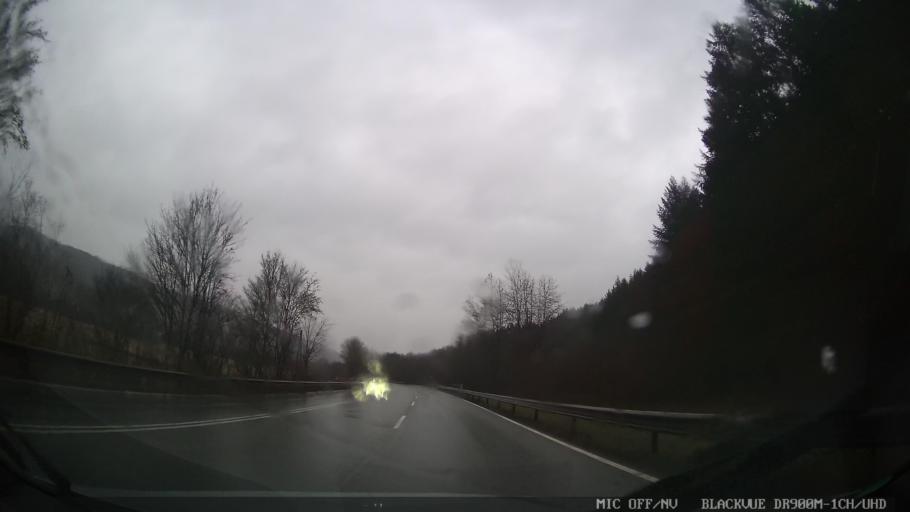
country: DE
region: Rheinland-Pfalz
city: Barenbach
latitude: 49.7545
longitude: 7.4344
